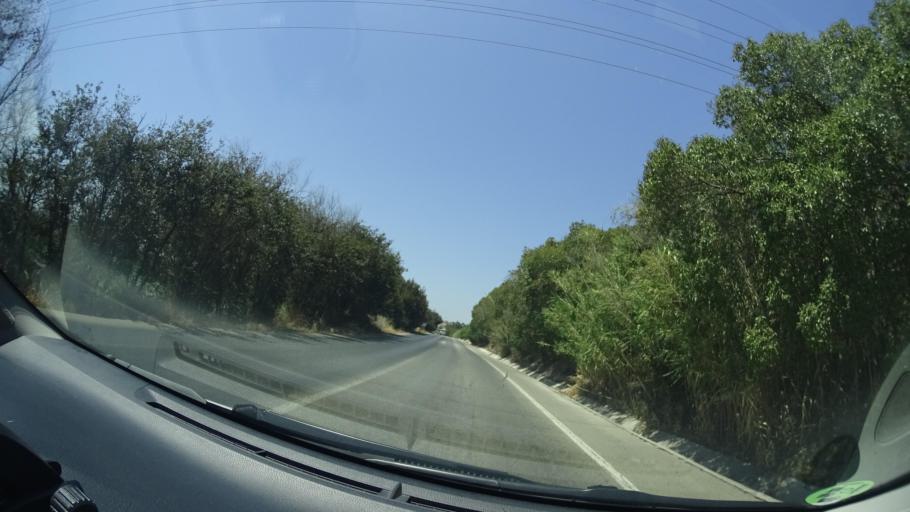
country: ES
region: Andalusia
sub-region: Provincia de Cadiz
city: Jerez de la Frontera
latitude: 36.6561
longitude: -6.0945
